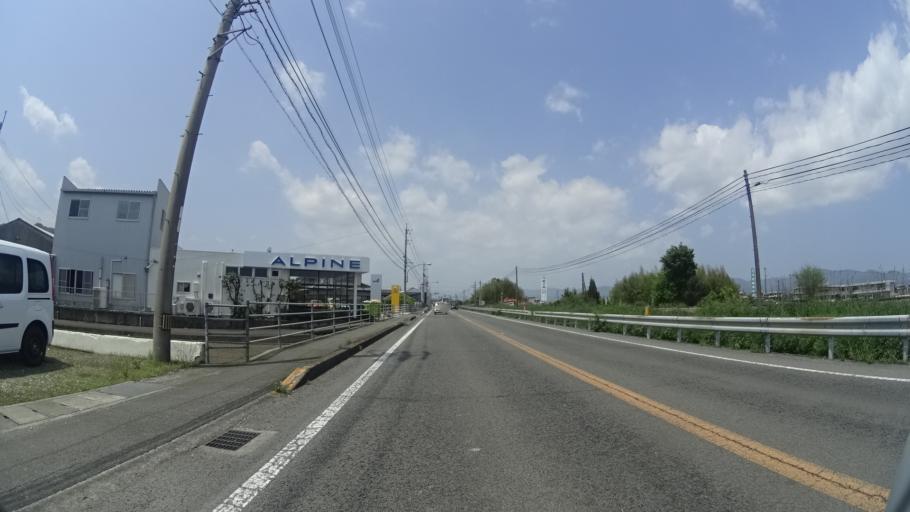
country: JP
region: Tokushima
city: Ishii
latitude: 34.0657
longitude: 134.4298
